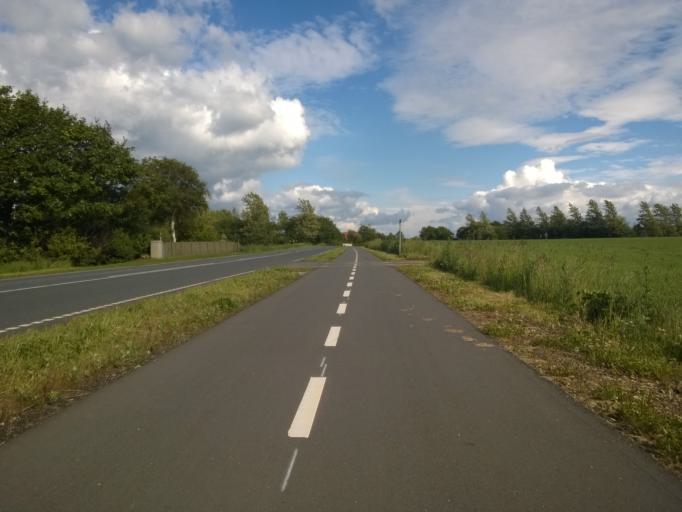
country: DK
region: Central Jutland
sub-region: Holstebro Kommune
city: Vinderup
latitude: 56.4606
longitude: 8.8567
